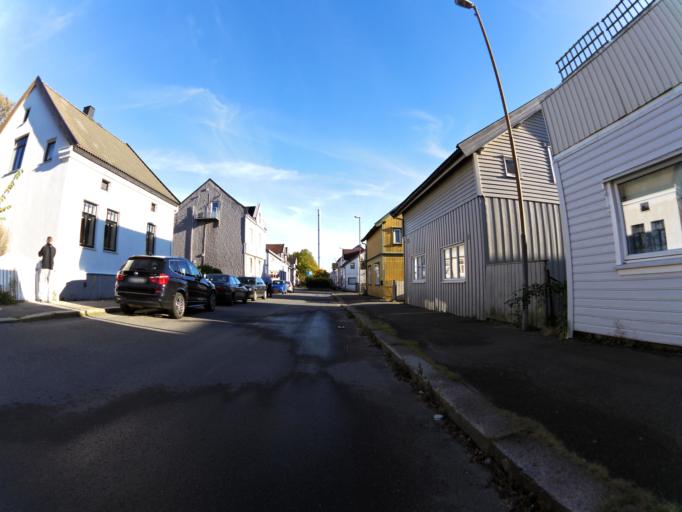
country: NO
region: Ostfold
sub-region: Sarpsborg
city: Sarpsborg
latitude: 59.2793
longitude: 11.1197
